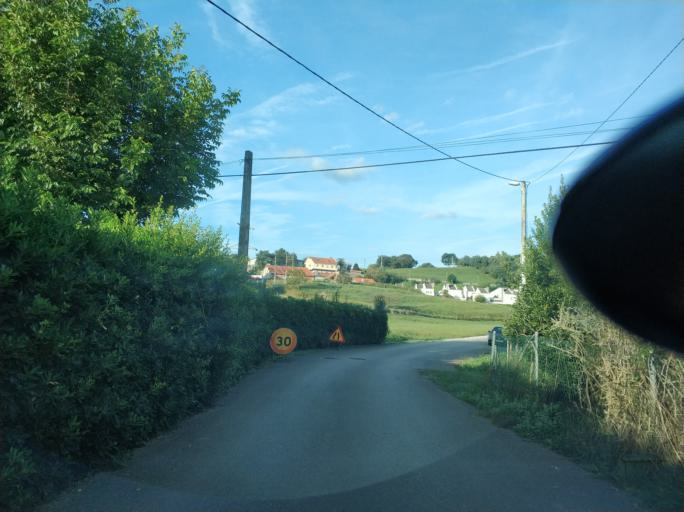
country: ES
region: Cantabria
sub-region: Provincia de Cantabria
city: Miengo
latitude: 43.4053
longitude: -3.9521
